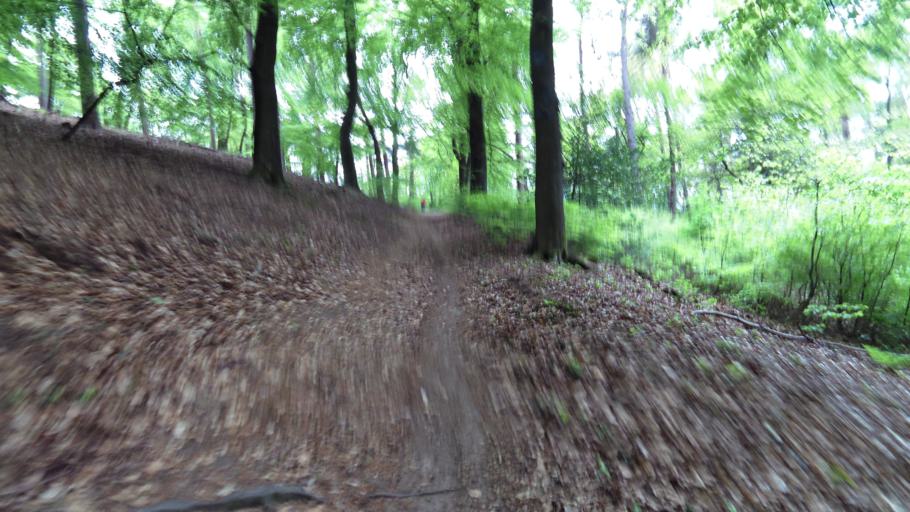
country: NL
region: Gelderland
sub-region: Gemeente Rheden
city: Velp
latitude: 52.0133
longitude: 5.9902
